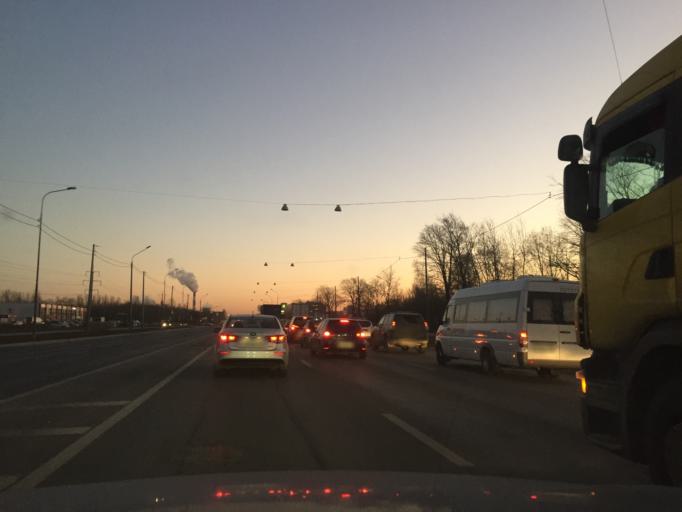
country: RU
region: St.-Petersburg
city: Obukhovo
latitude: 59.8545
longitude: 30.4243
